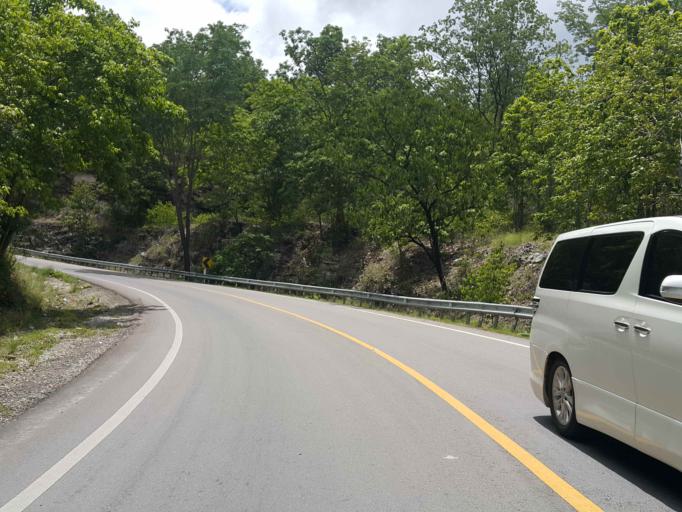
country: TH
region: Chiang Mai
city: Chom Thong
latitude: 18.5005
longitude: 98.6715
